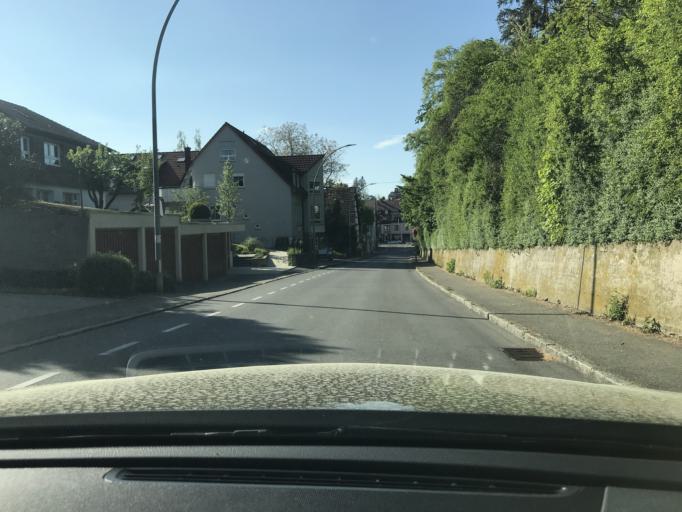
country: DE
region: Baden-Wuerttemberg
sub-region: Regierungsbezirk Stuttgart
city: Weinstadt-Endersbach
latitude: 48.8113
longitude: 9.3669
